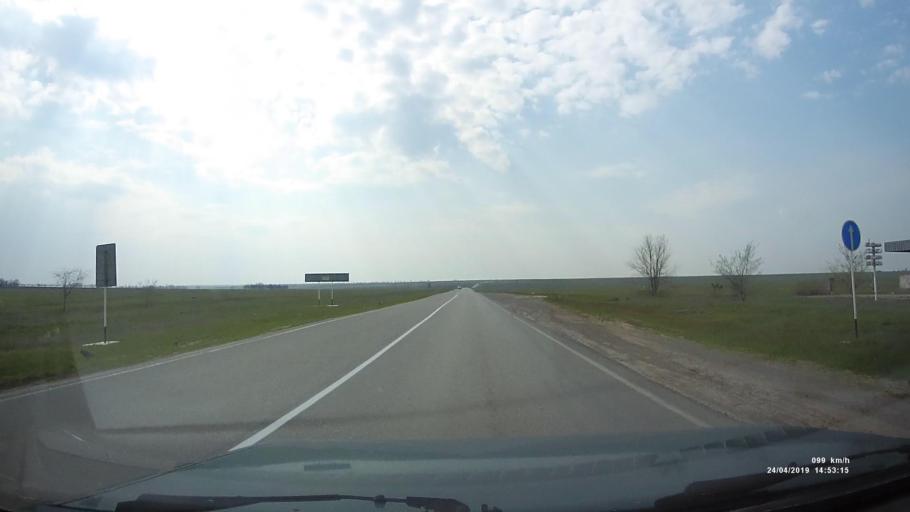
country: RU
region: Rostov
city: Remontnoye
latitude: 46.5312
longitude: 43.6631
